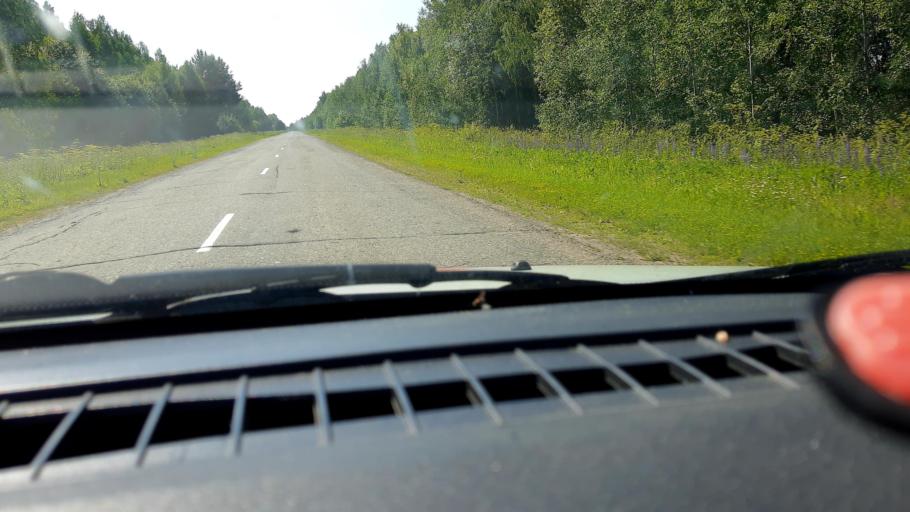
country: RU
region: Nizjnij Novgorod
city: Sharanga
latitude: 57.0769
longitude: 46.5384
